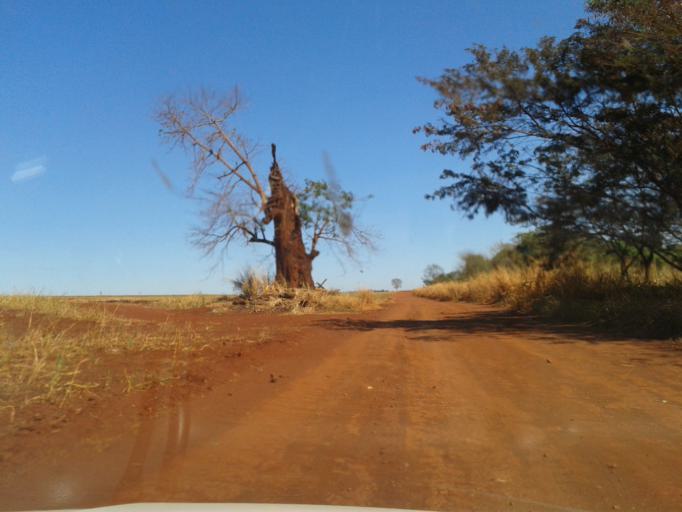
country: BR
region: Minas Gerais
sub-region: Centralina
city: Centralina
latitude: -18.5898
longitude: -49.1538
